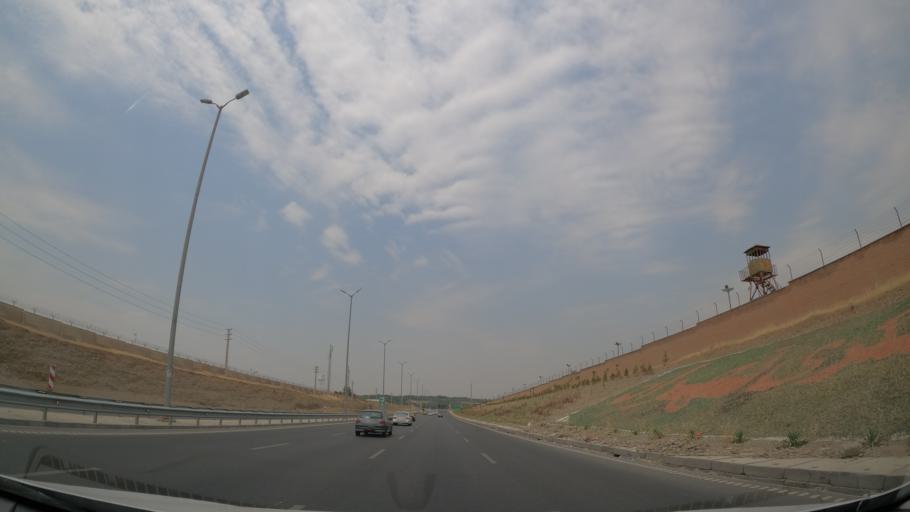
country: IR
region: Tehran
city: Shahr-e Qods
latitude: 35.7399
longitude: 51.2293
